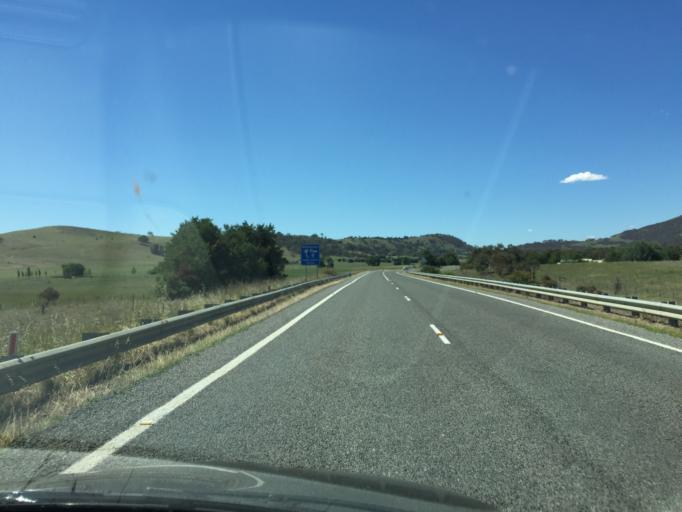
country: AU
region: Australian Capital Territory
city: Macarthur
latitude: -35.7066
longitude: 149.1583
